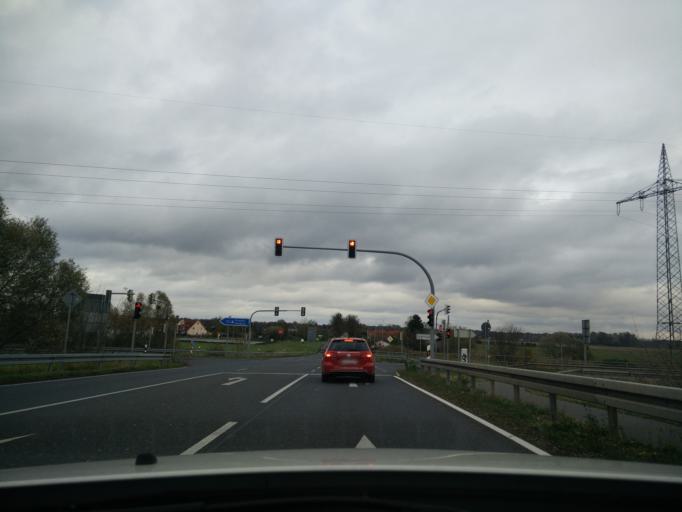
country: DE
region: Brandenburg
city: Brieselang
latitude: 52.5735
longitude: 12.9740
